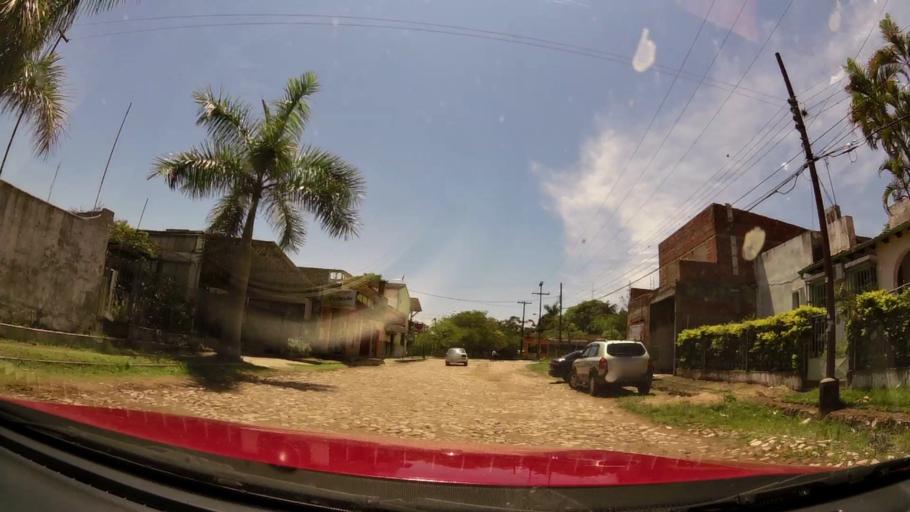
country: PY
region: Central
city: Colonia Mariano Roque Alonso
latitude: -25.1936
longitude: -57.5482
